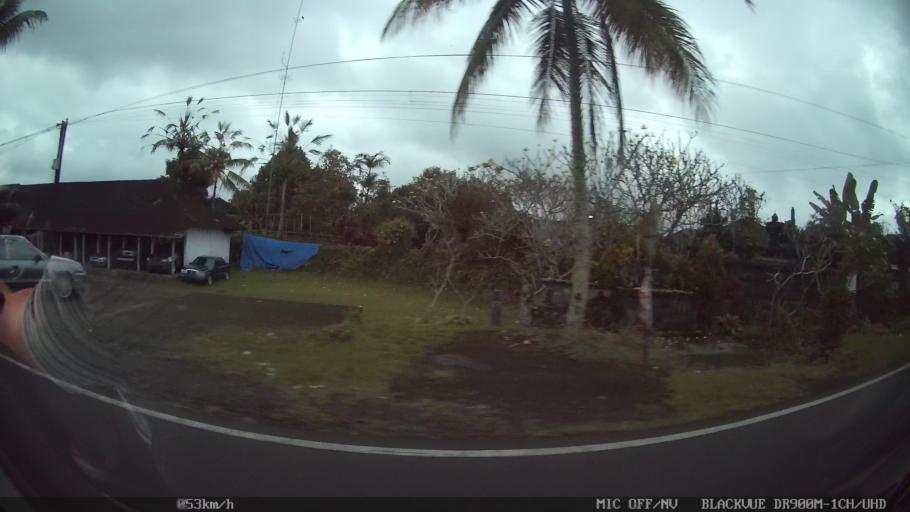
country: ID
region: Bali
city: Empalan
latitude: -8.3964
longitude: 115.1506
